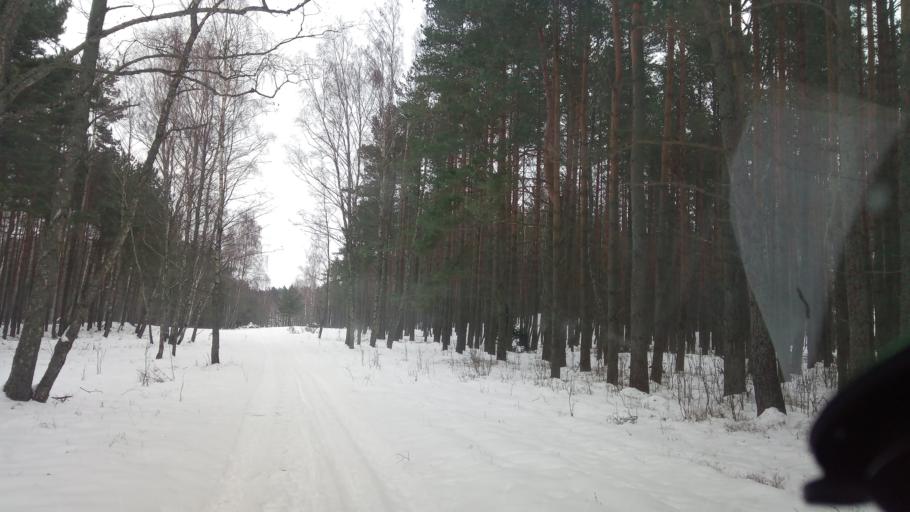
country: LT
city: Neringa
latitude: 55.4194
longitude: 21.1046
